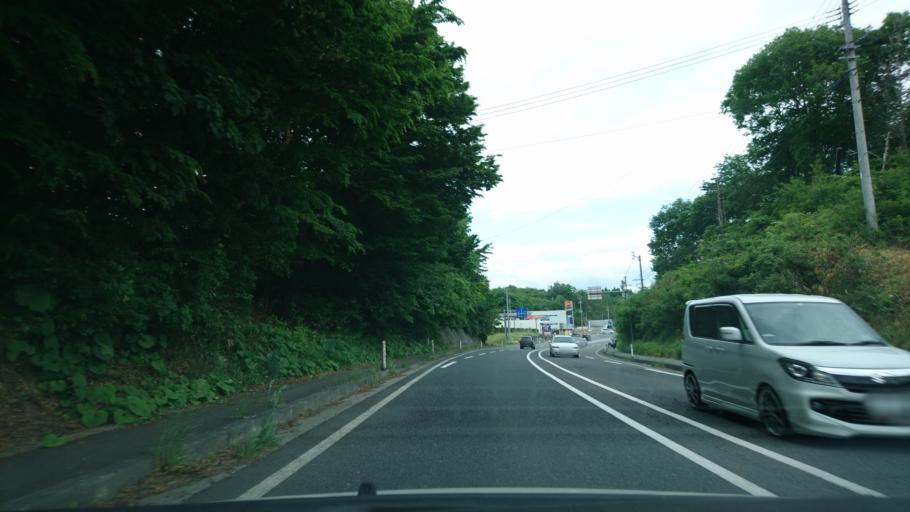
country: JP
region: Iwate
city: Ichinoseki
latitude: 38.9088
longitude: 141.1631
